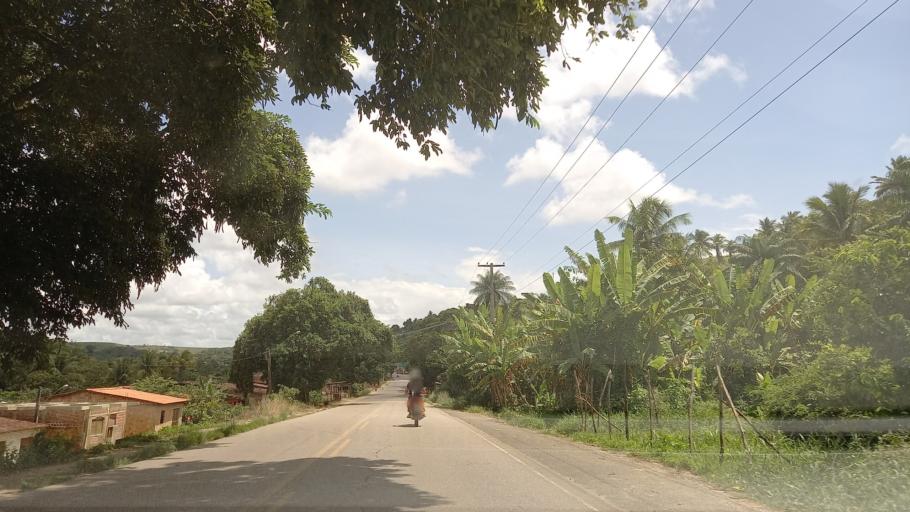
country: BR
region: Pernambuco
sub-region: Rio Formoso
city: Rio Formoso
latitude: -8.6561
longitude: -35.1498
